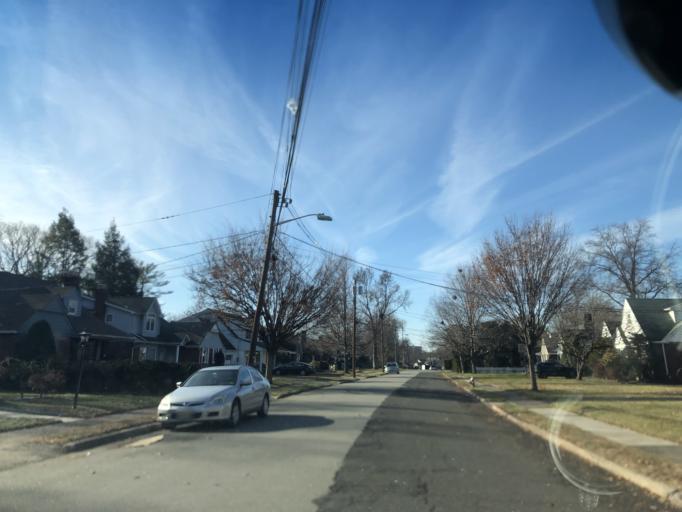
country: US
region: New Jersey
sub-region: Bergen County
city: Fair Lawn
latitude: 40.9247
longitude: -74.1251
